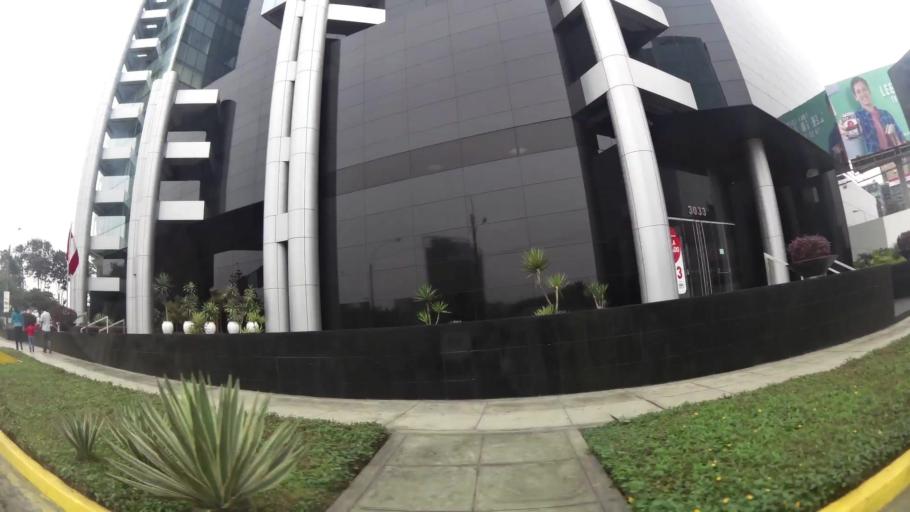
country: PE
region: Lima
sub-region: Lima
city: San Luis
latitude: -12.0934
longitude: -77.0231
